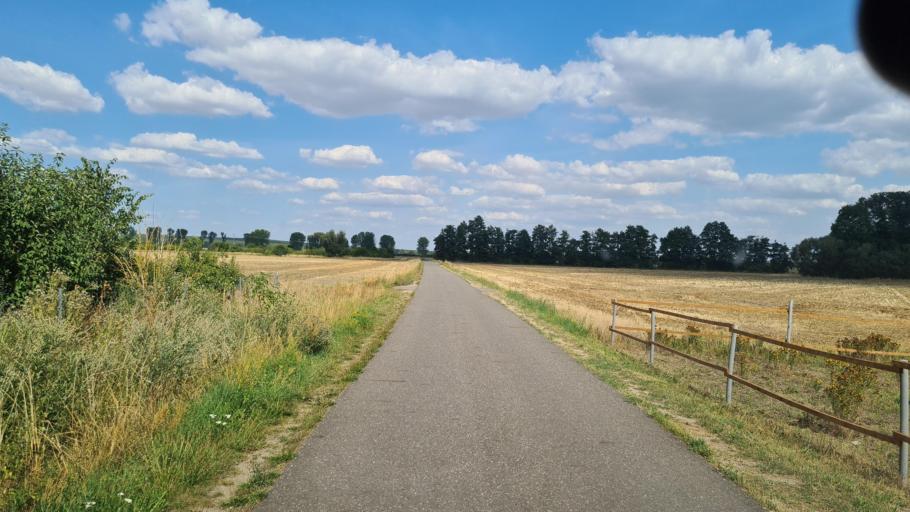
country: DE
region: Saxony-Anhalt
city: Elster
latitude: 51.8716
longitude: 12.8214
